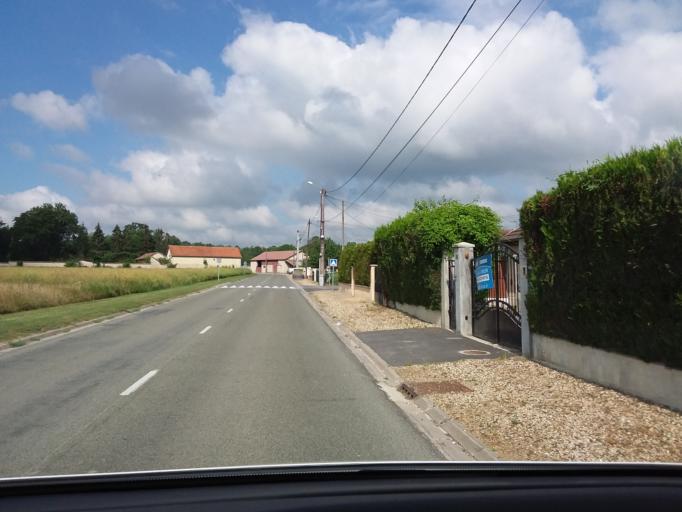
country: FR
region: Champagne-Ardenne
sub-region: Departement de la Marne
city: Cormicy
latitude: 49.4077
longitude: 3.8169
